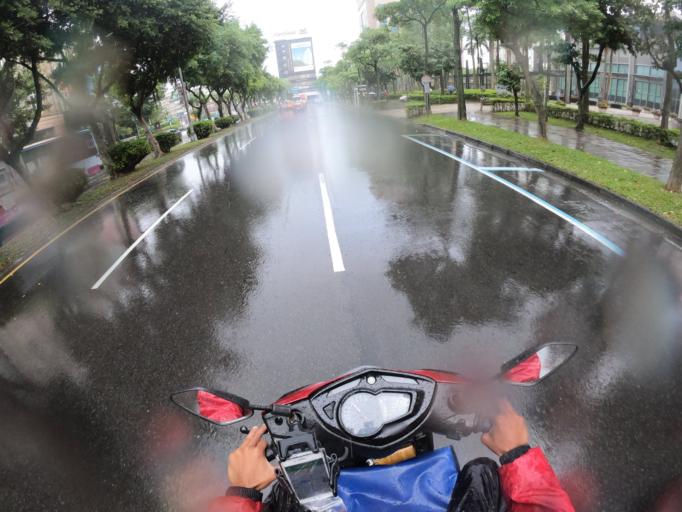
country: TW
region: Taipei
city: Taipei
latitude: 25.0395
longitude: 121.5686
